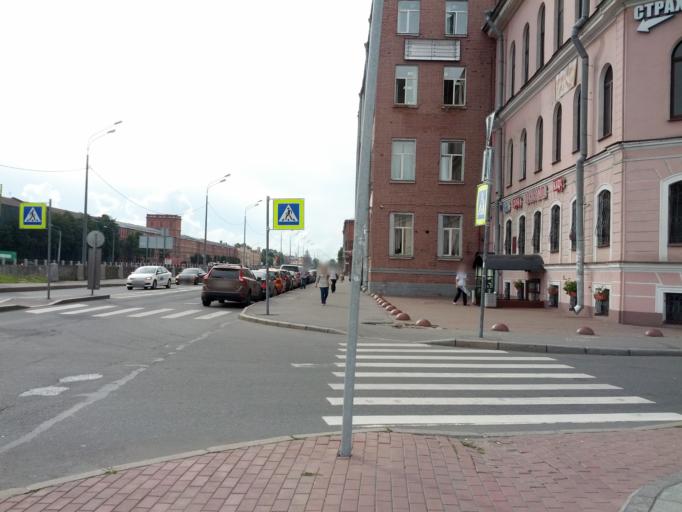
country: RU
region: St.-Petersburg
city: Admiralteisky
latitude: 59.9095
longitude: 30.2879
